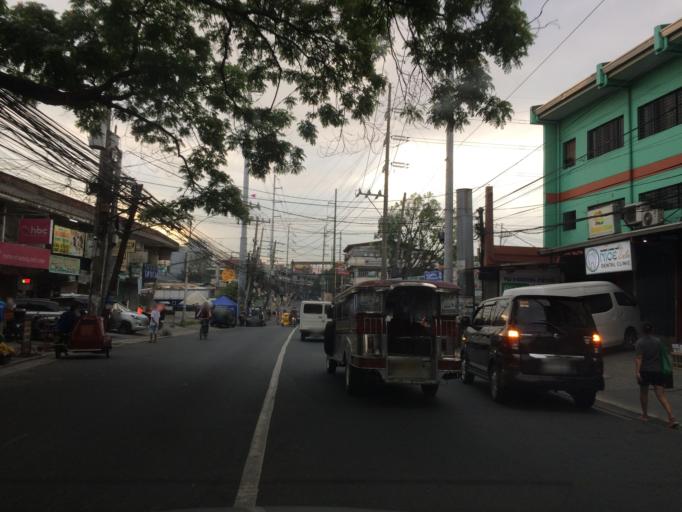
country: PH
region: Calabarzon
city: Bagong Pagasa
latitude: 14.6763
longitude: 121.0430
